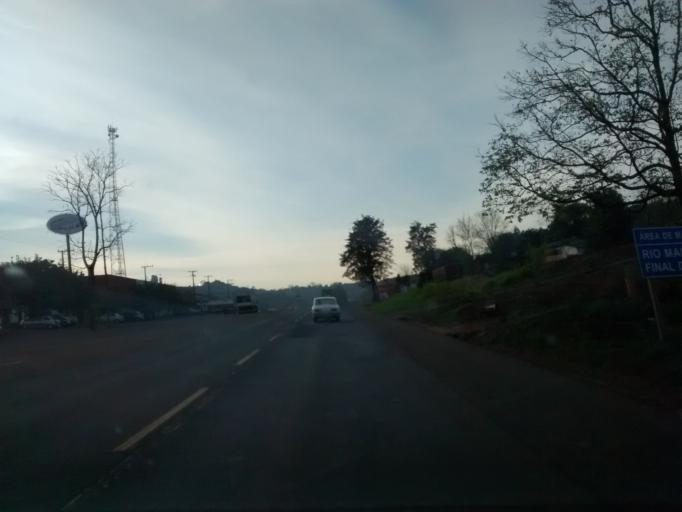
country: BR
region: Parana
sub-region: Francisco Beltrao
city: Francisco Beltrao
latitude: -26.1123
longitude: -53.0487
